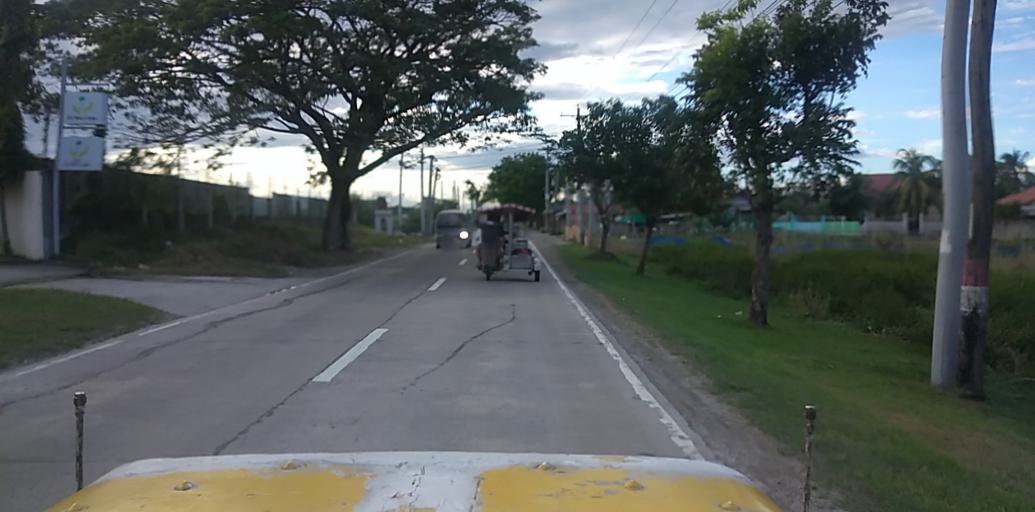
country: PH
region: Central Luzon
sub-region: Province of Pampanga
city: San Antonio
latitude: 15.1569
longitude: 120.7084
